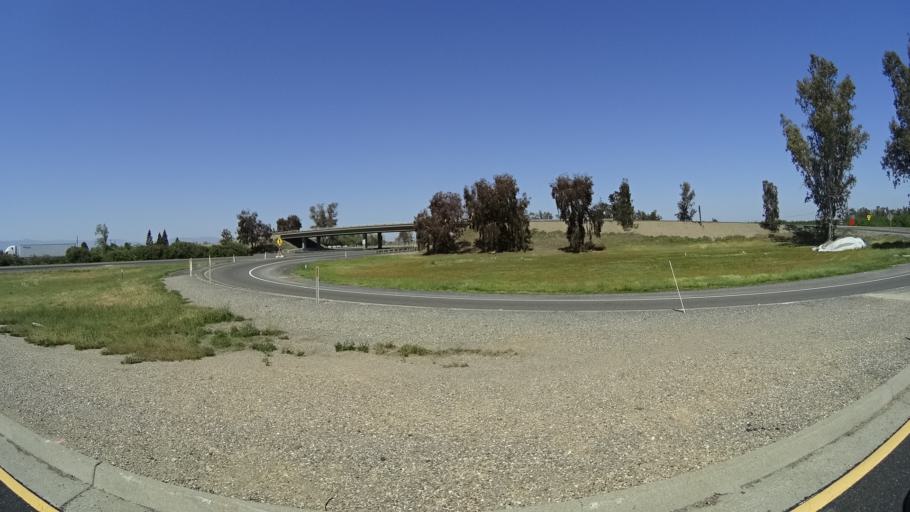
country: US
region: California
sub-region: Glenn County
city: Willows
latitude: 39.5813
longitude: -122.2094
